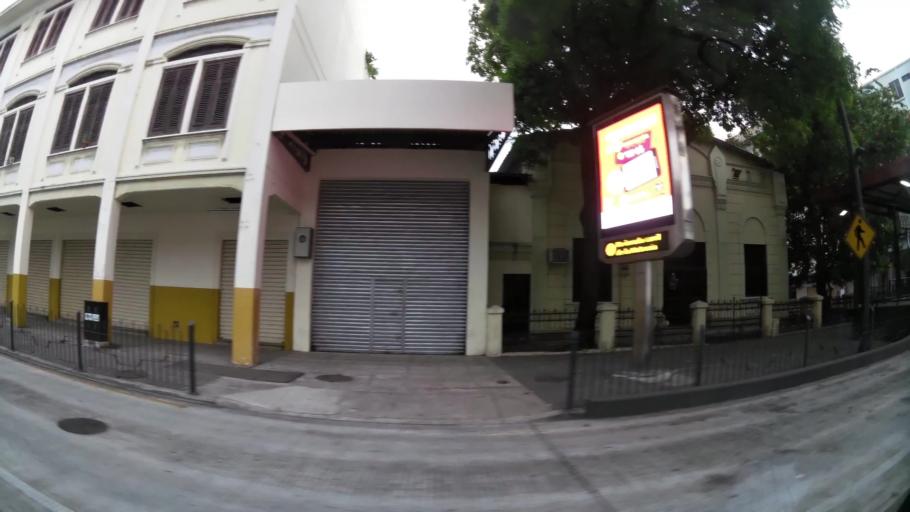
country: EC
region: Guayas
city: Guayaquil
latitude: -2.2090
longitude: -79.8858
